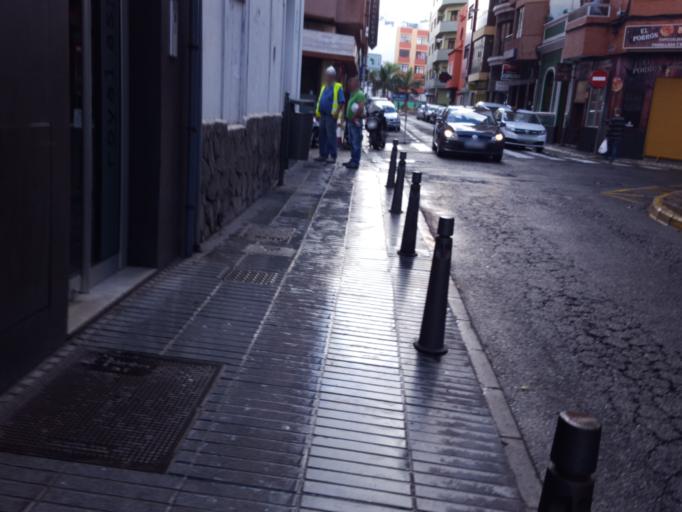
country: ES
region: Canary Islands
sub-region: Provincia de Las Palmas
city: Las Palmas de Gran Canaria
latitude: 28.1384
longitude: -15.4355
